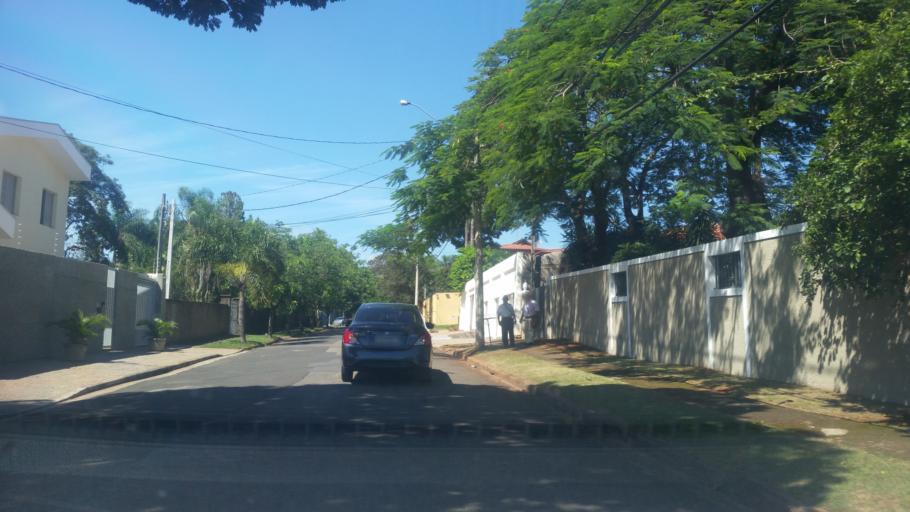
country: BR
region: Sao Paulo
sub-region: Campinas
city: Campinas
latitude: -22.8578
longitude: -47.0494
